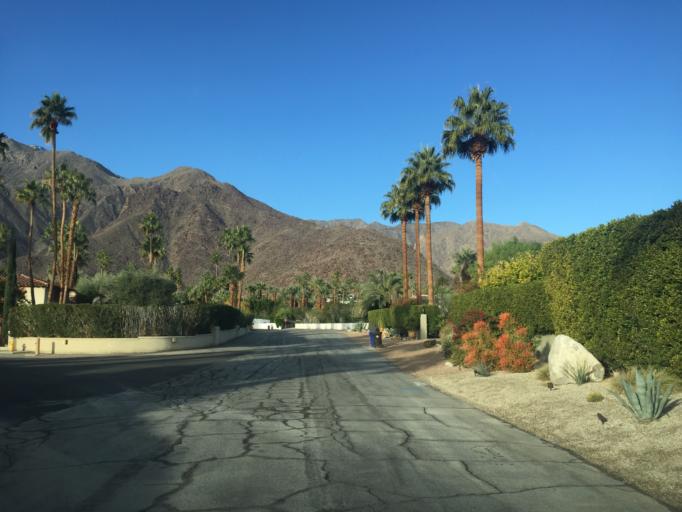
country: US
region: California
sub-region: Riverside County
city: Palm Springs
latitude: 33.8421
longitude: -116.5525
